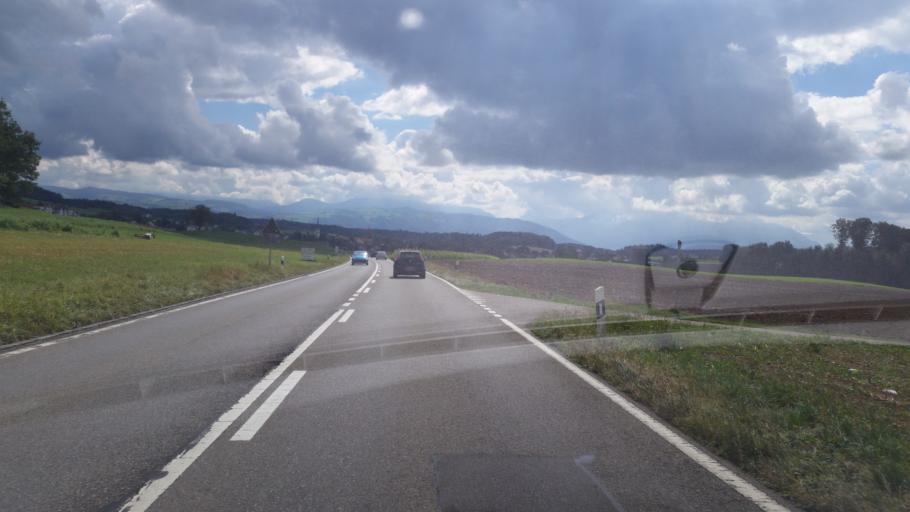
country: CH
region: Zurich
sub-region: Bezirk Affoltern
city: Mettmenstetten
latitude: 47.2548
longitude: 8.4521
